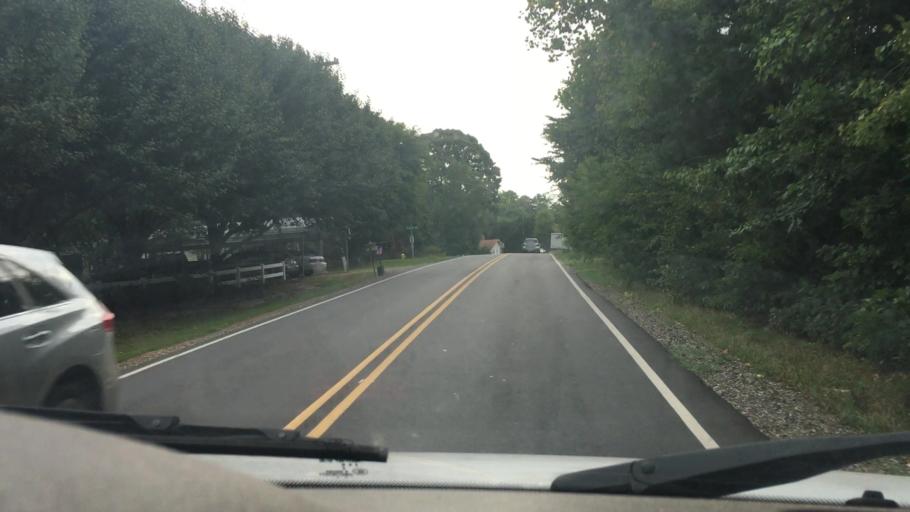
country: US
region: North Carolina
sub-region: Gaston County
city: Davidson
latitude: 35.5428
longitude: -80.8441
